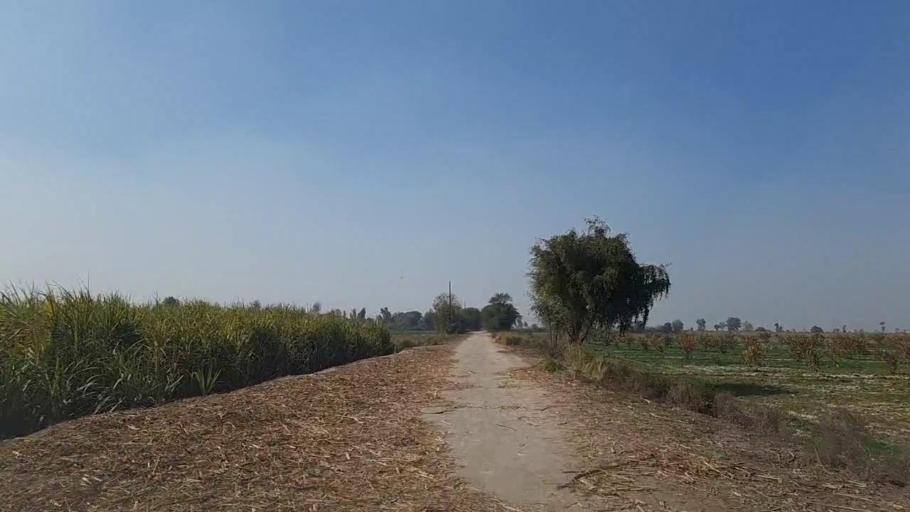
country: PK
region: Sindh
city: Daur
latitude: 26.5097
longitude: 68.3459
